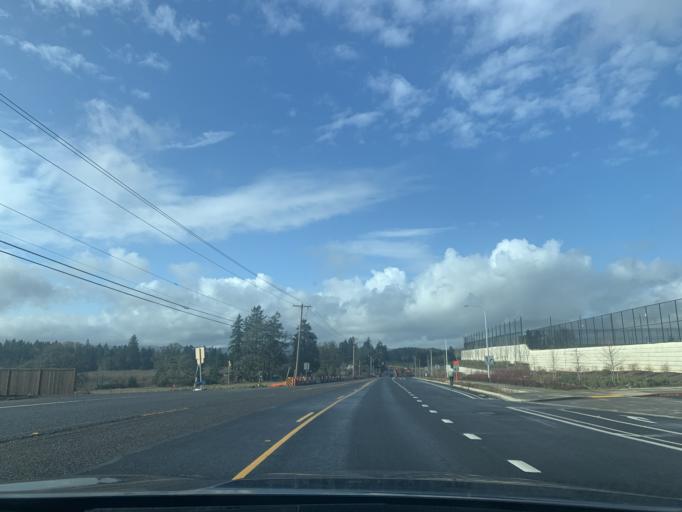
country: US
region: Oregon
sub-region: Washington County
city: King City
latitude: 45.4260
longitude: -122.8564
